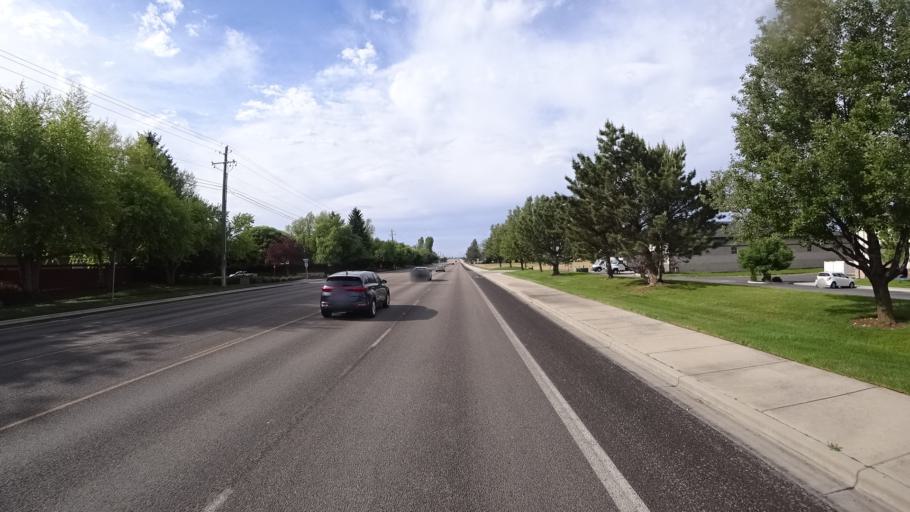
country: US
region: Idaho
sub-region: Ada County
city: Meridian
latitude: 43.6003
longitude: -116.3746
